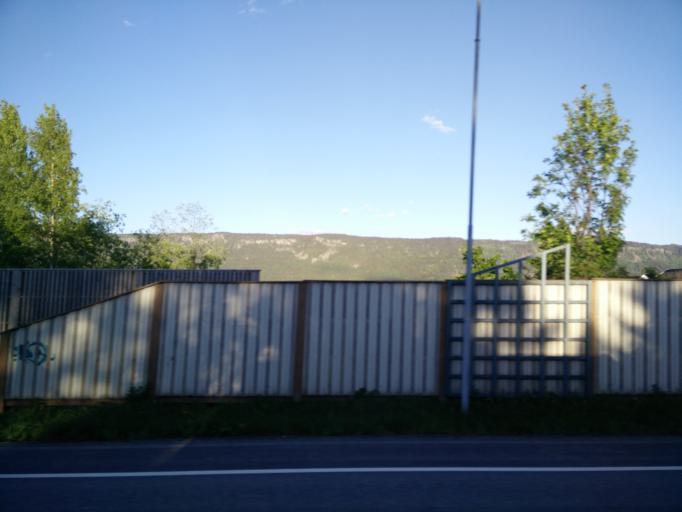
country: NO
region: Buskerud
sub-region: Hole
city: Vik
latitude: 60.0886
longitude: 10.2880
